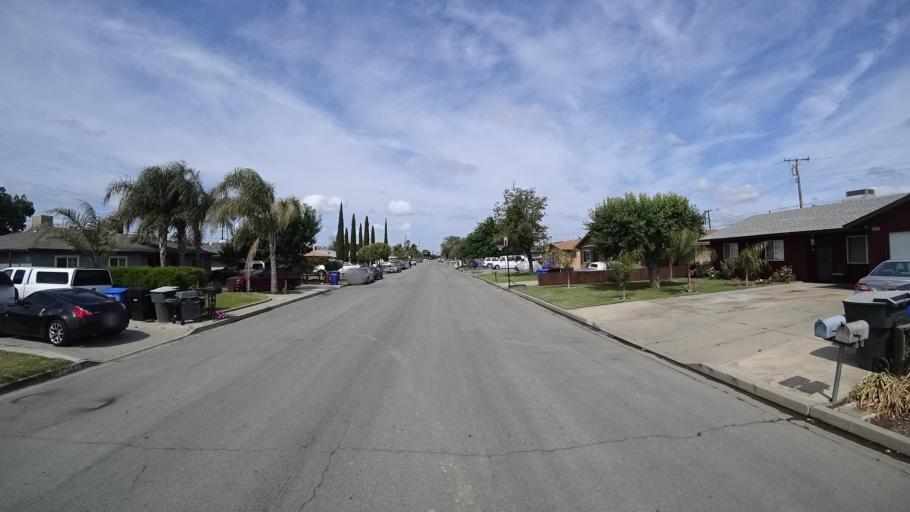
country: US
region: California
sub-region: Kings County
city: Home Garden
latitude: 36.3057
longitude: -119.6515
